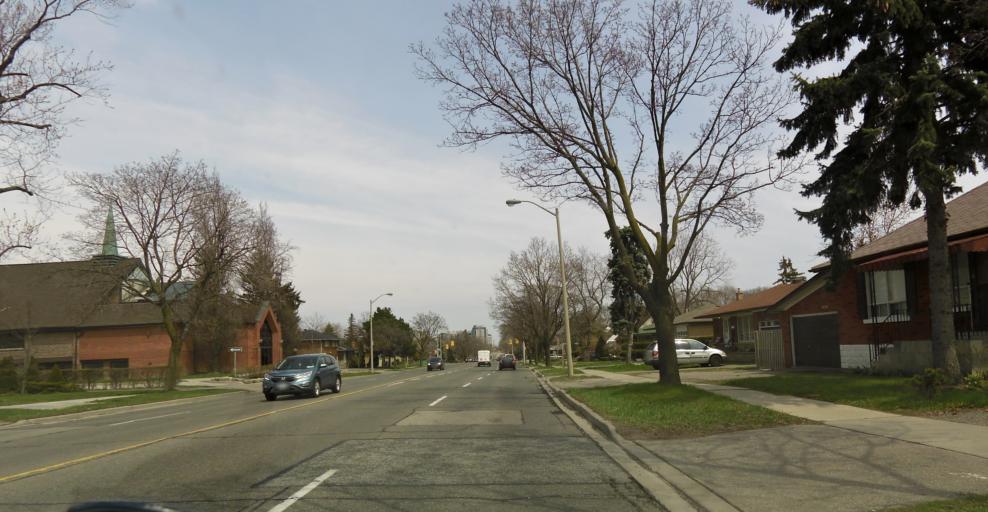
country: CA
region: Ontario
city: Etobicoke
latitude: 43.6385
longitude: -79.5495
